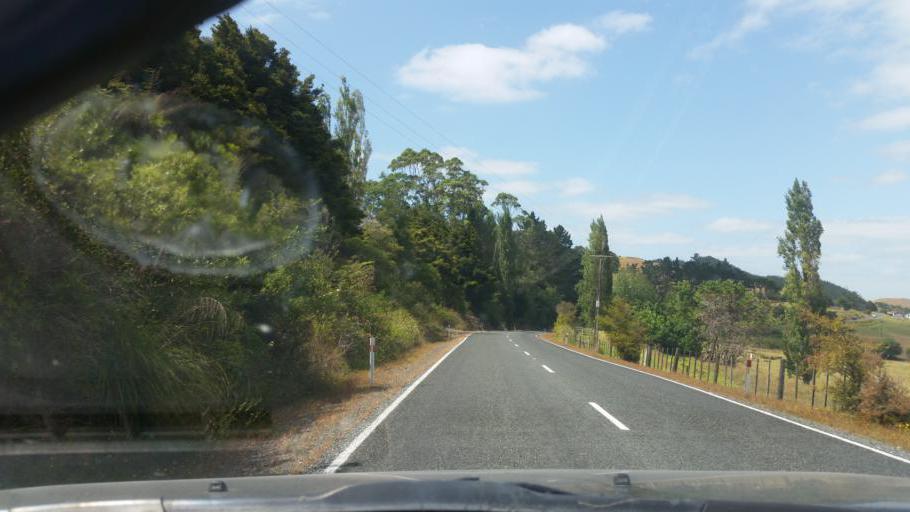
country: NZ
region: Northland
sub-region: Whangarei
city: Ruakaka
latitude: -35.9464
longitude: 174.2925
